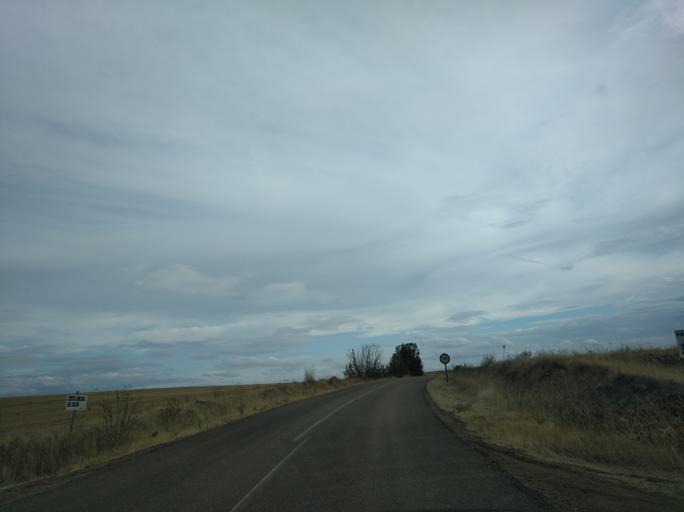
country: ES
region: Extremadura
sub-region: Provincia de Badajoz
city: Badajoz
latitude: 38.9003
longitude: -7.0166
